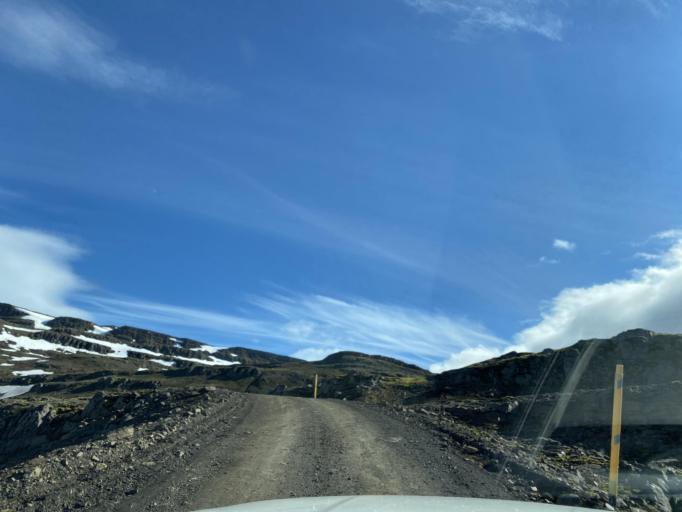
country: IS
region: East
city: Eskifjoerdur
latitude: 65.1688
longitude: -14.1288
